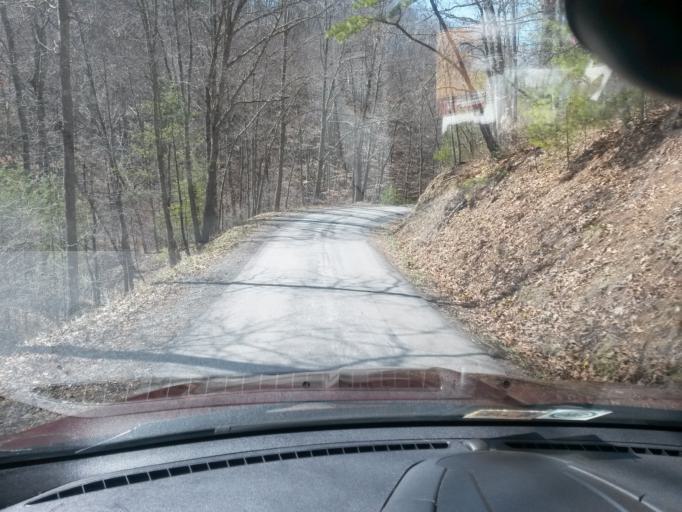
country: US
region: West Virginia
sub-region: Greenbrier County
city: White Sulphur Springs
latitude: 37.6801
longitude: -80.3325
